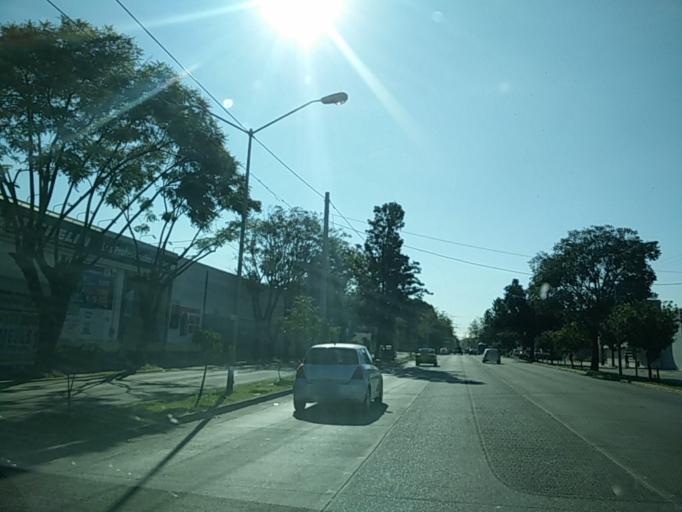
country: MX
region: Jalisco
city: Guadalajara
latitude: 20.6529
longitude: -103.3432
